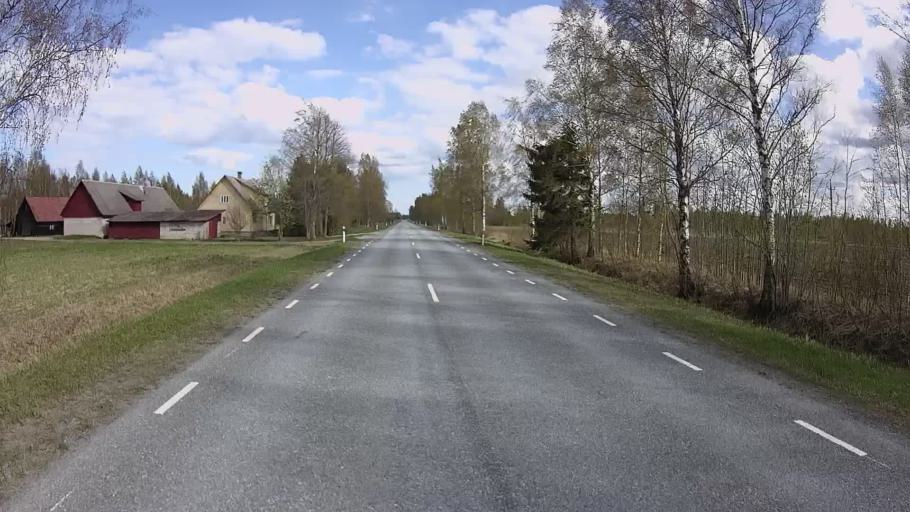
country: EE
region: Jogevamaa
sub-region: Mustvee linn
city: Mustvee
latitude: 58.7905
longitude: 26.9529
